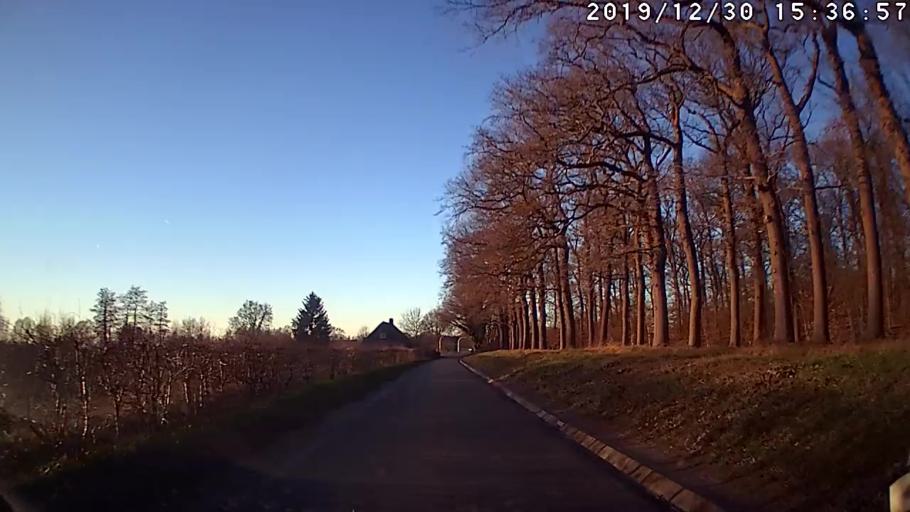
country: NL
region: Overijssel
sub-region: Gemeente Raalte
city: Heino
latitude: 52.4556
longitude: 6.1814
